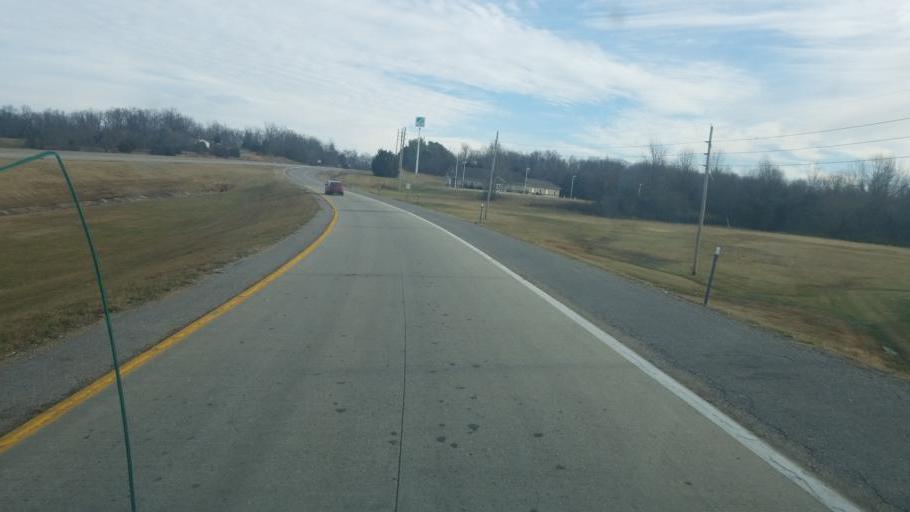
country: US
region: Missouri
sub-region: Stoddard County
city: Dexter
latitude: 36.8088
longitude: -89.9689
